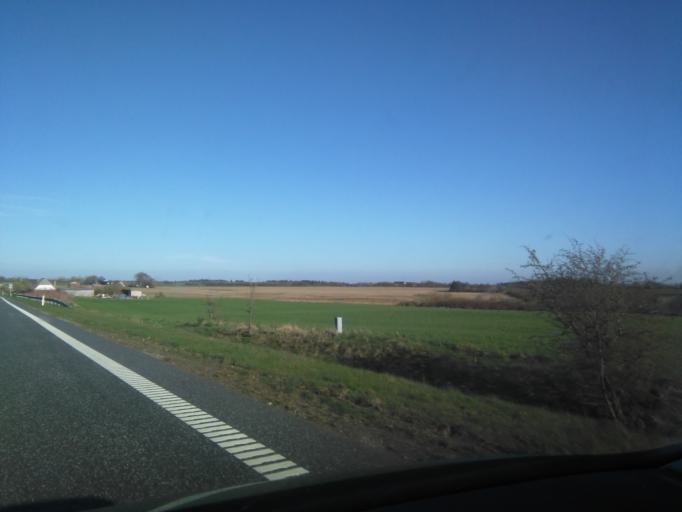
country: DK
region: Central Jutland
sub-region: Ringkobing-Skjern Kommune
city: Videbaek
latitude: 56.0890
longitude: 8.5654
